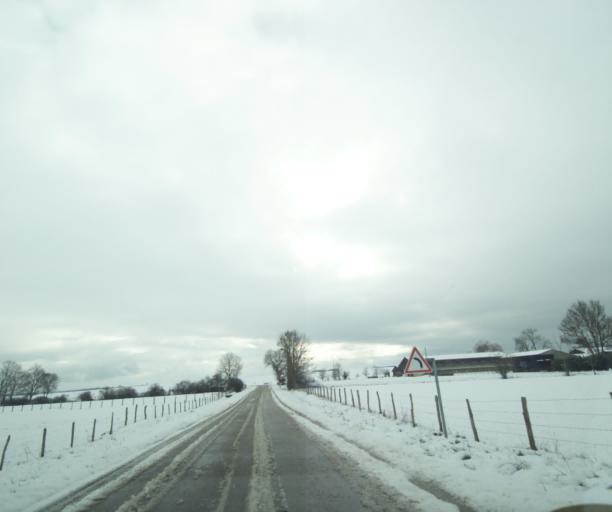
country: FR
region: Champagne-Ardenne
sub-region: Departement de la Haute-Marne
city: Montier-en-Der
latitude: 48.4511
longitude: 4.6958
